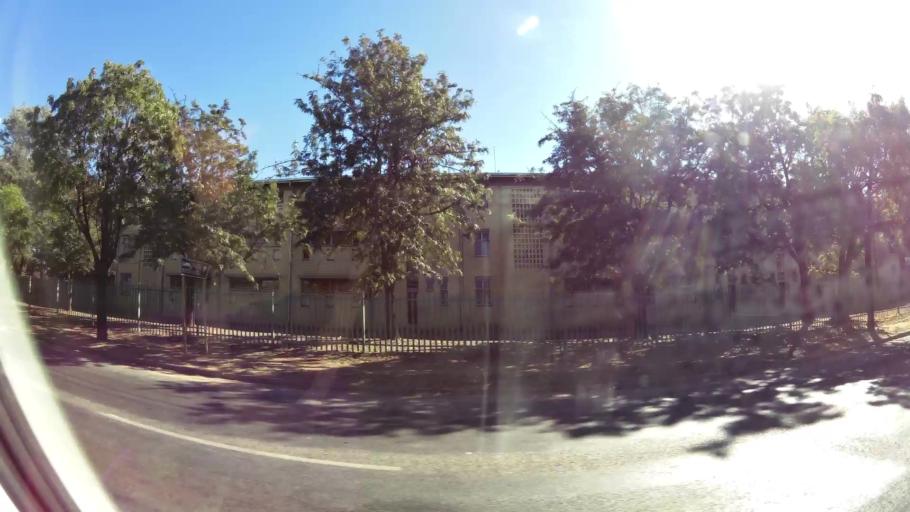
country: ZA
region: Limpopo
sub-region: Capricorn District Municipality
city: Polokwane
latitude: -23.9072
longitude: 29.4745
